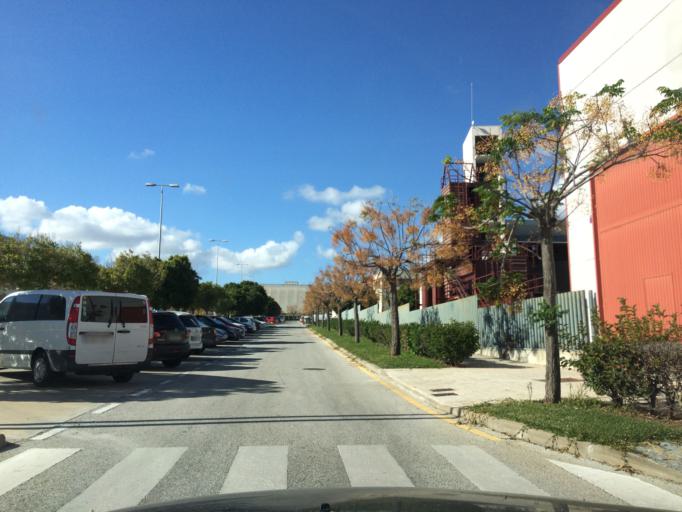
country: ES
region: Andalusia
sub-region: Provincia de Malaga
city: Alhaurin de la Torre
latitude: 36.7332
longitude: -4.5448
